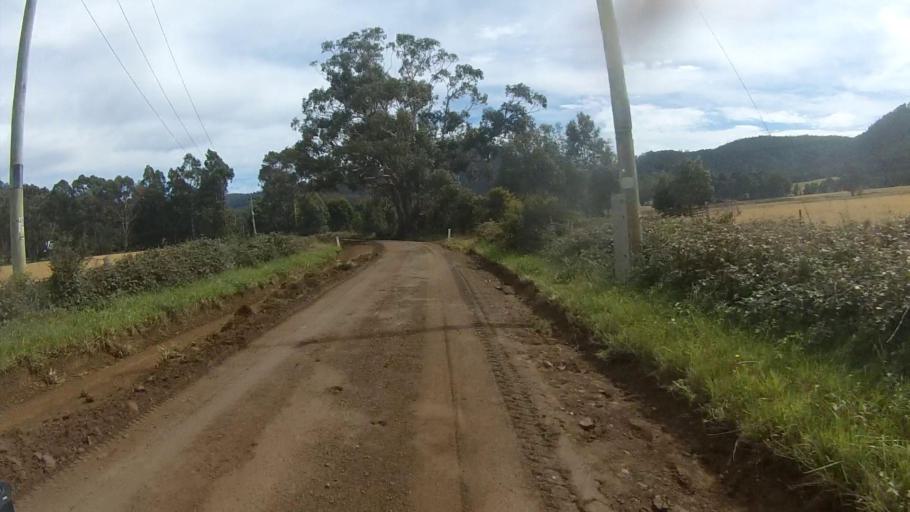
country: AU
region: Tasmania
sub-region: Sorell
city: Sorell
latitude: -42.7742
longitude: 147.8090
